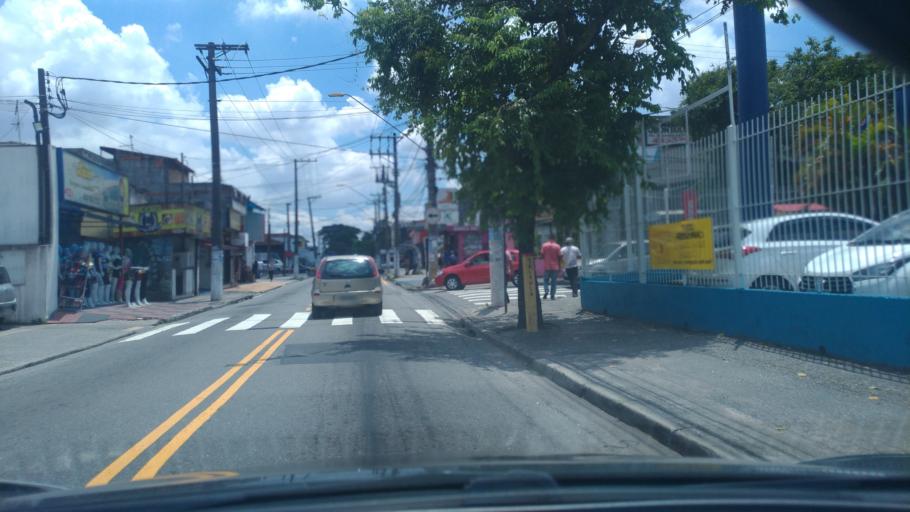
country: BR
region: Sao Paulo
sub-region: Santo Andre
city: Santo Andre
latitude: -23.6934
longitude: -46.5059
